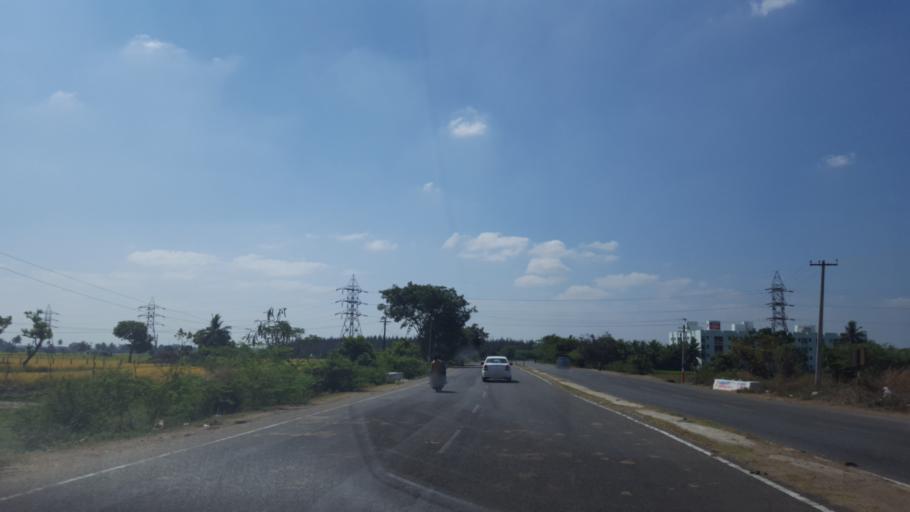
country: IN
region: Tamil Nadu
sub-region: Kancheepuram
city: Mamallapuram
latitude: 12.7115
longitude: 80.1863
